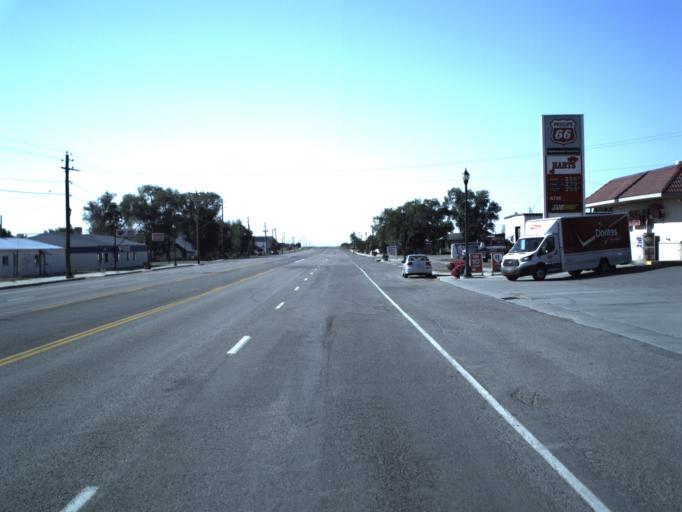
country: US
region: Utah
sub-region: Emery County
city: Huntington
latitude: 39.3243
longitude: -110.9646
